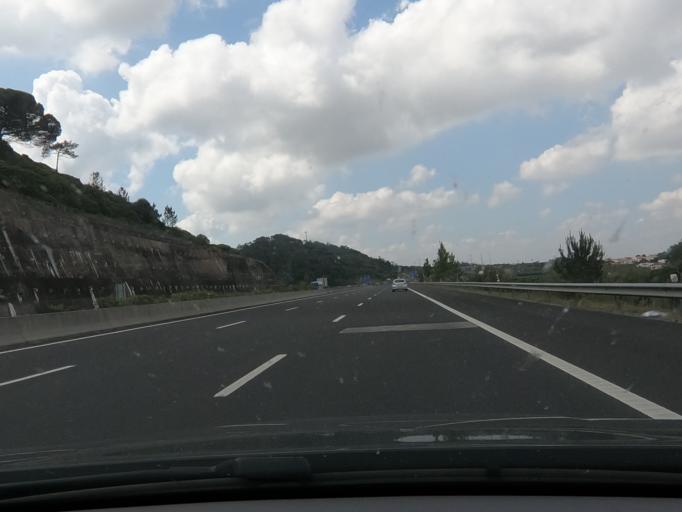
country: PT
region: Leiria
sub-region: Caldas da Rainha
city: Caldas da Rainha
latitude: 39.4533
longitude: -9.1200
